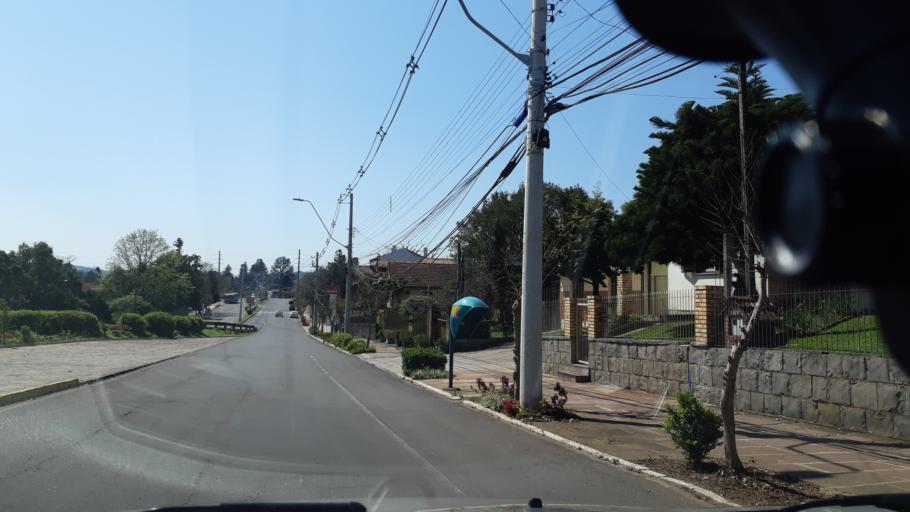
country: BR
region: Rio Grande do Sul
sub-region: Nova Petropolis
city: Nova Petropolis
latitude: -29.3838
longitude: -51.1194
